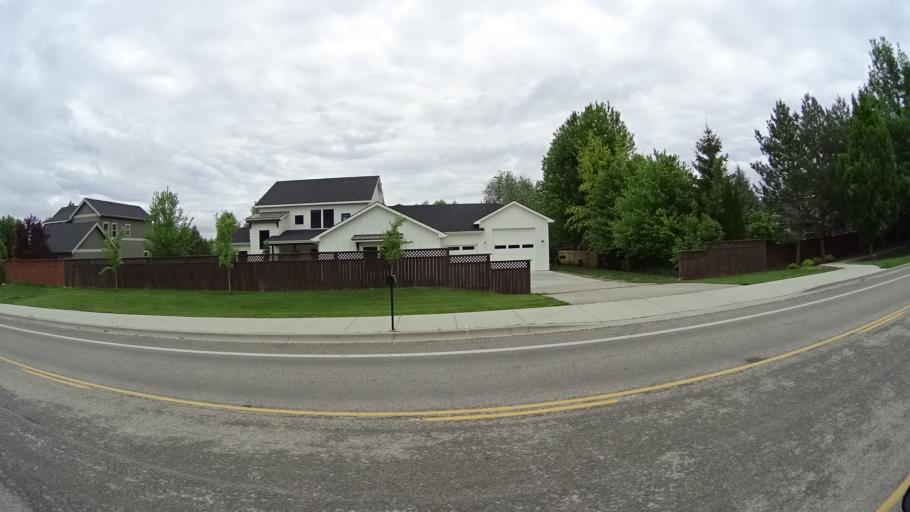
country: US
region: Idaho
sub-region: Ada County
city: Eagle
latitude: 43.7065
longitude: -116.3479
